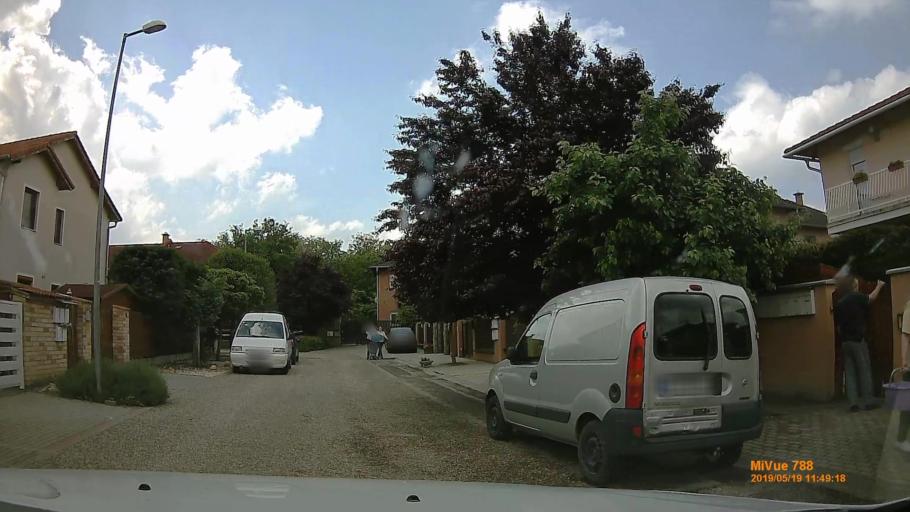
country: HU
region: Budapest
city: Budapest XVII. keruelet
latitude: 47.4686
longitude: 19.2239
